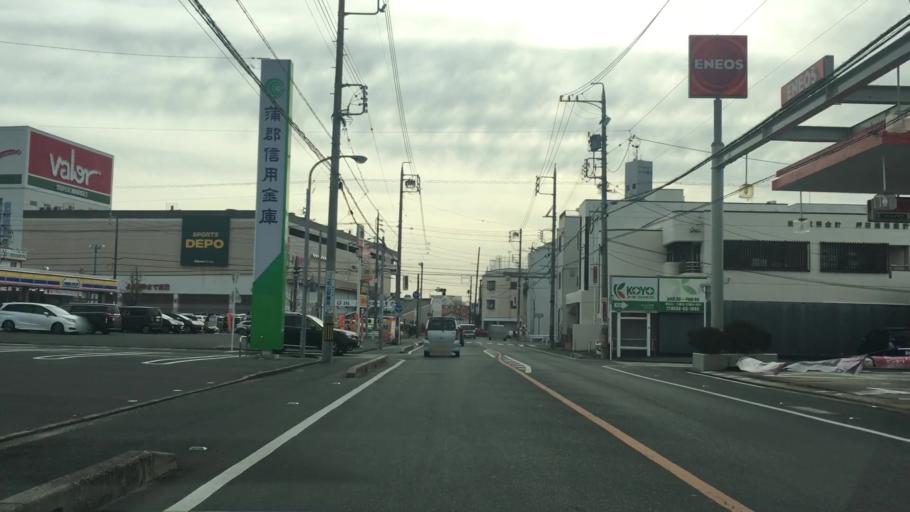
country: JP
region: Aichi
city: Toyohashi
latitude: 34.7556
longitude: 137.3935
